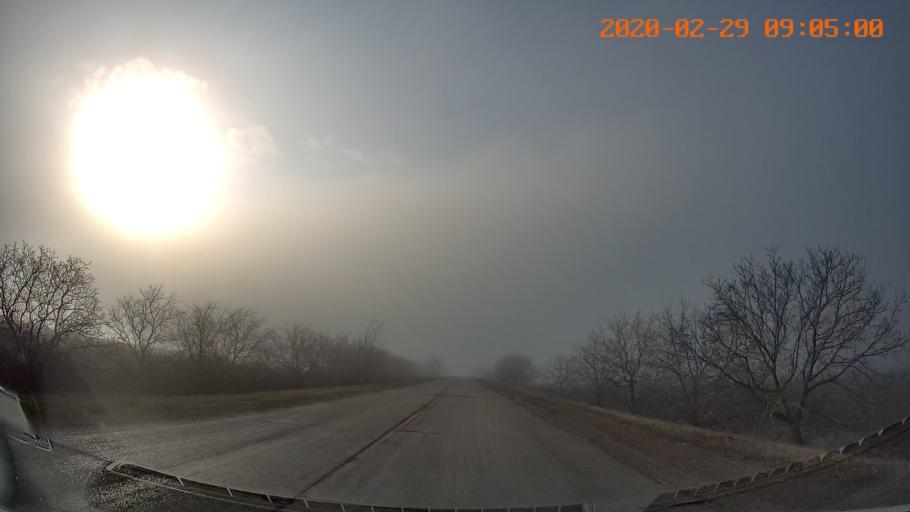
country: MD
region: Telenesti
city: Tiraspolul Nou
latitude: 46.8948
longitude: 29.7385
